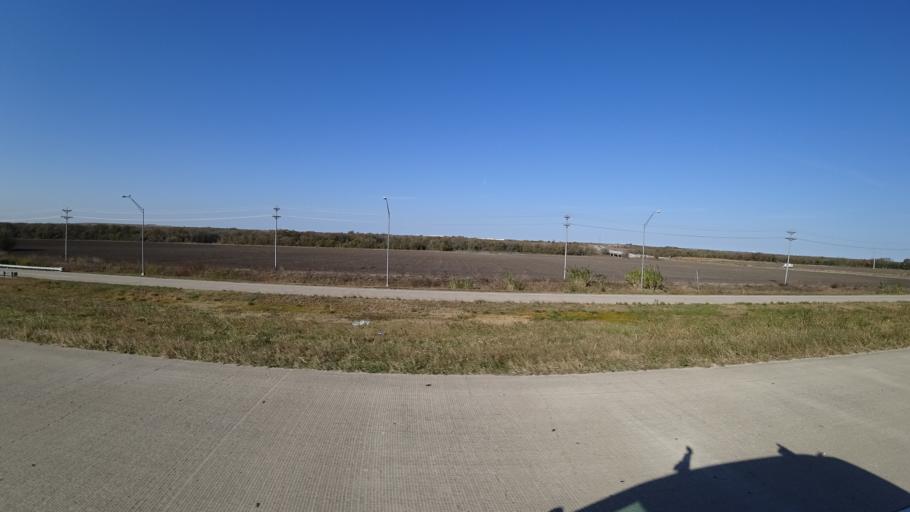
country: US
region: Texas
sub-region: Travis County
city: Manor
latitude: 30.3678
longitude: -97.5841
